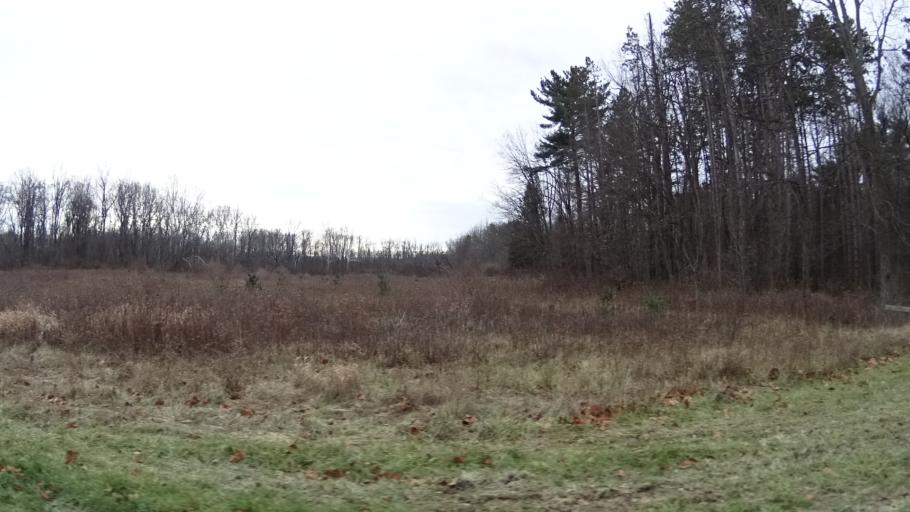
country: US
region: Ohio
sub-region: Lorain County
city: Wellington
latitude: 41.1484
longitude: -82.2468
